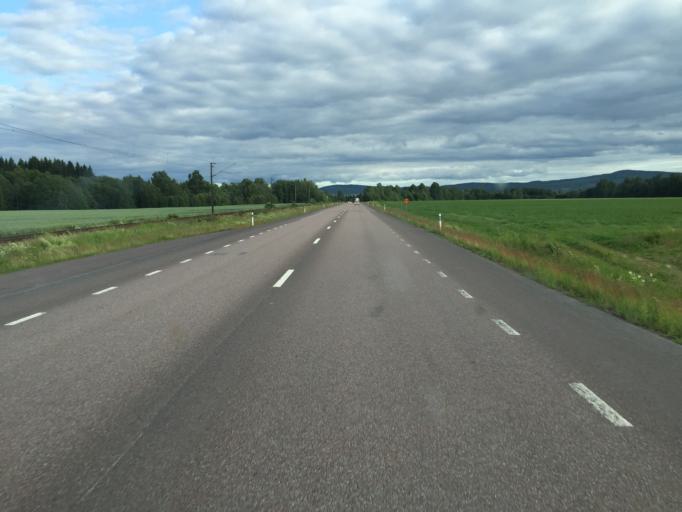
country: SE
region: Dalarna
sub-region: Gagnefs Kommun
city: Djuras
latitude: 60.5745
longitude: 15.1234
